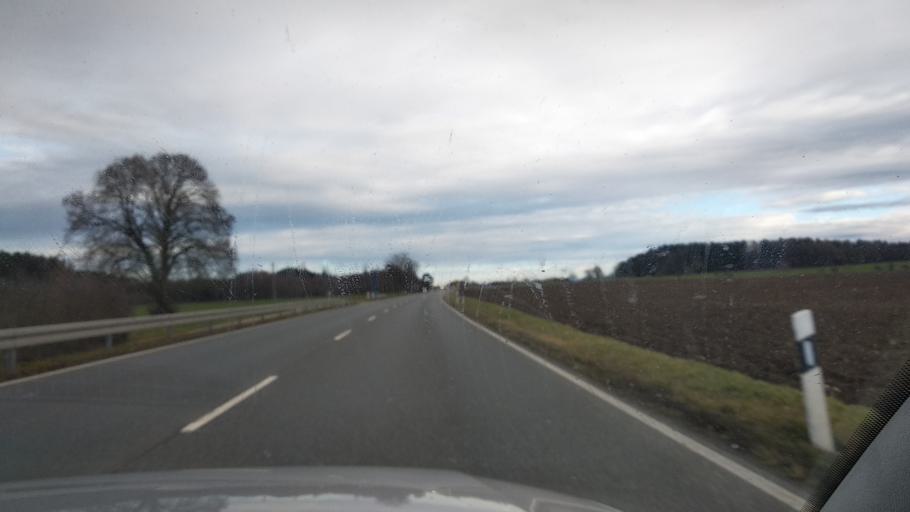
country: DE
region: Bavaria
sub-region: Upper Bavaria
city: Kirchseeon
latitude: 48.0693
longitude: 11.9215
